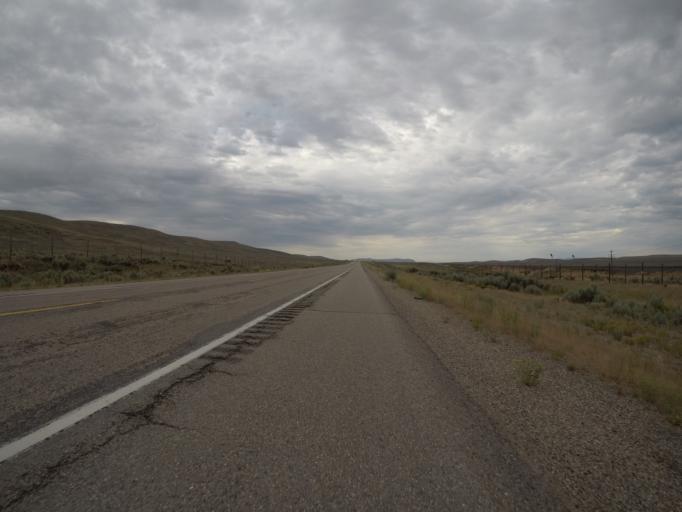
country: US
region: Utah
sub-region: Rich County
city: Randolph
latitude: 41.8400
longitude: -110.9767
